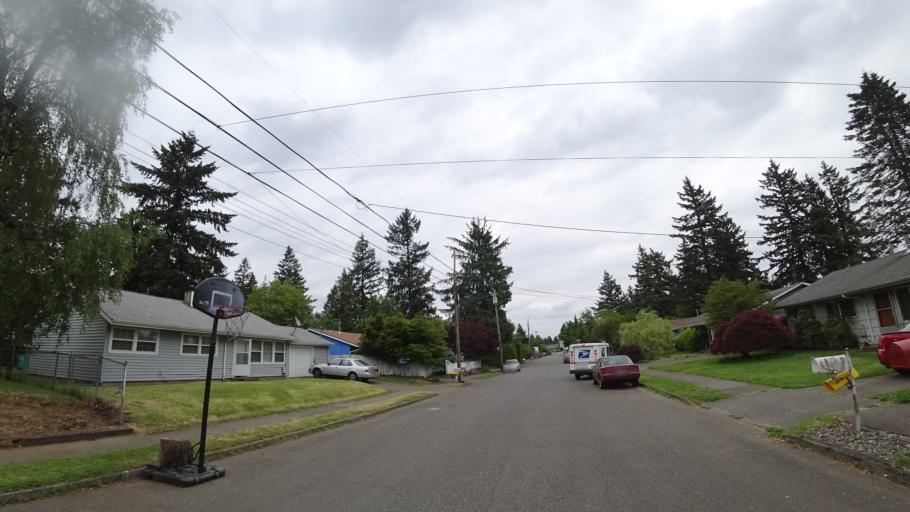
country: US
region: Oregon
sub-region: Multnomah County
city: Lents
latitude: 45.5108
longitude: -122.5333
